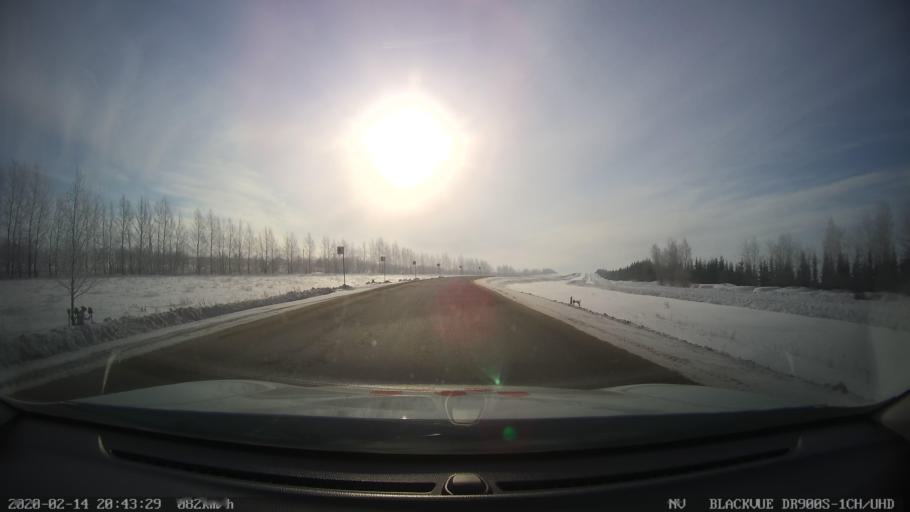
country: RU
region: Tatarstan
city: Kuybyshevskiy Zaton
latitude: 55.3074
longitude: 49.1482
